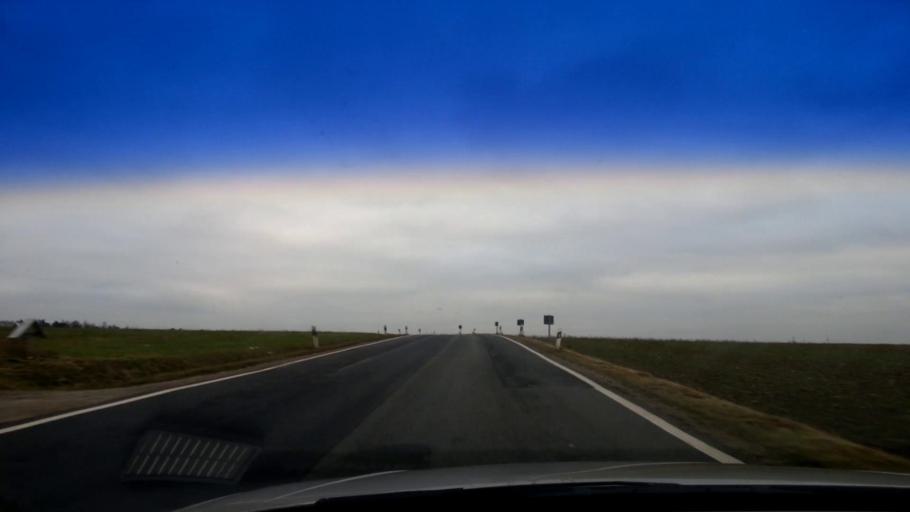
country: DE
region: Bavaria
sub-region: Upper Franconia
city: Burgebrach
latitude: 49.8038
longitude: 10.7827
